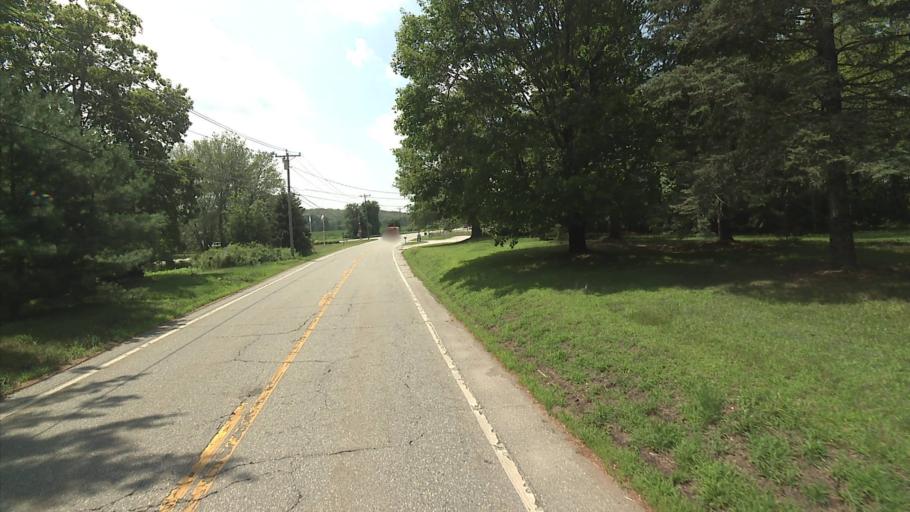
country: US
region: Connecticut
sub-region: New London County
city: Preston City
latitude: 41.5290
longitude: -71.9791
